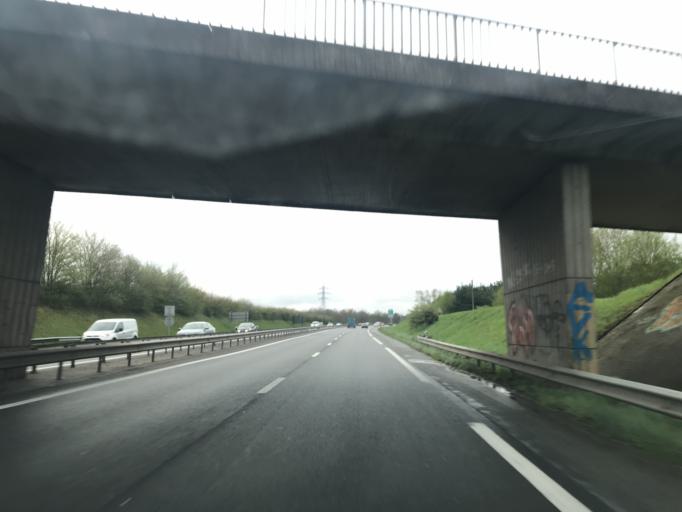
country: FR
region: Centre
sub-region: Departement du Loiret
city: Boigny-sur-Bionne
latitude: 47.9200
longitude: 2.0013
